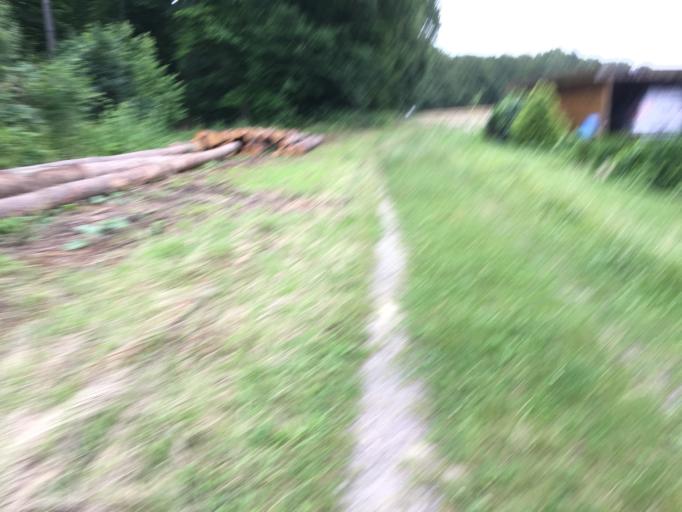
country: DE
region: North Rhine-Westphalia
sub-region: Regierungsbezirk Detmold
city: Lage
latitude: 51.9997
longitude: 8.8492
